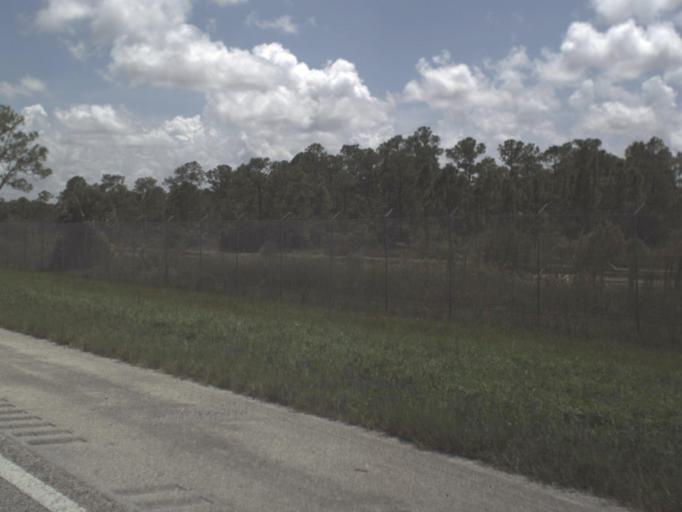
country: US
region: Florida
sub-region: Collier County
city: Immokalee
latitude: 26.1694
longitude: -81.0247
